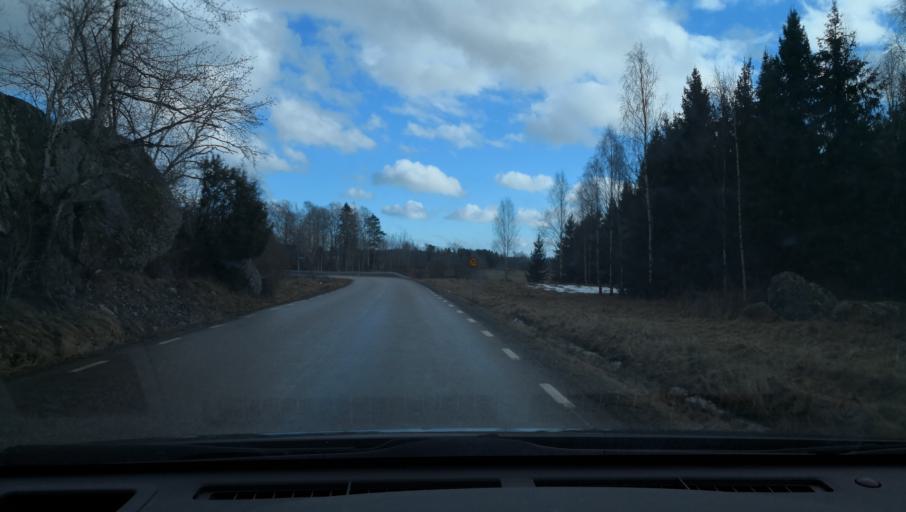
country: SE
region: OErebro
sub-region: Lindesbergs Kommun
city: Fellingsbro
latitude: 59.3509
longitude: 15.6772
